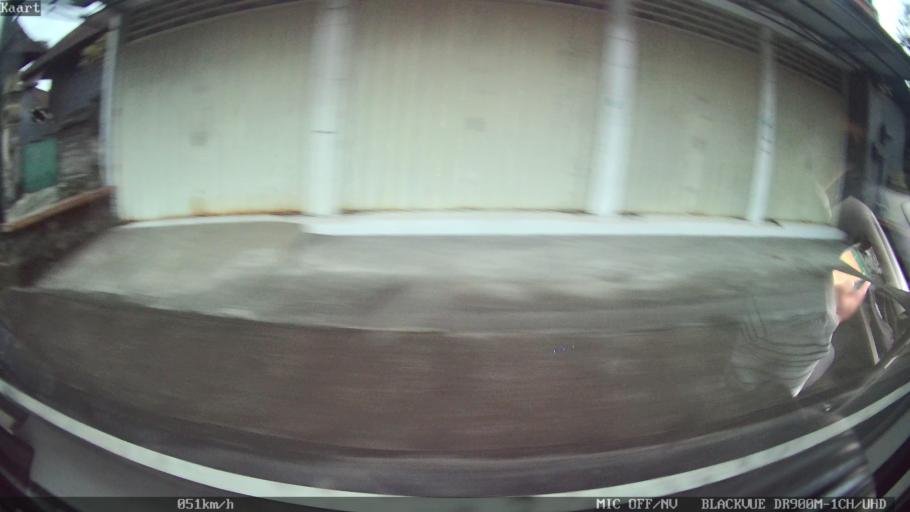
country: ID
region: Bali
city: Banjar Sayanbaleran
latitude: -8.5141
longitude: 115.1876
